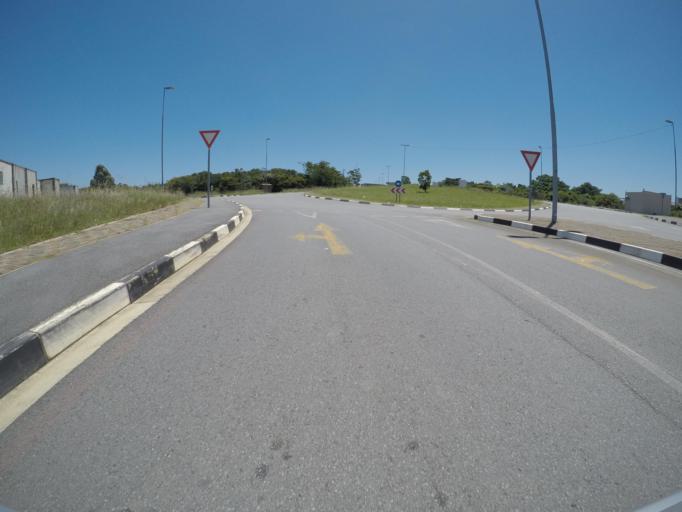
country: ZA
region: Eastern Cape
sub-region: Buffalo City Metropolitan Municipality
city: East London
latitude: -32.9502
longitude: 27.9451
